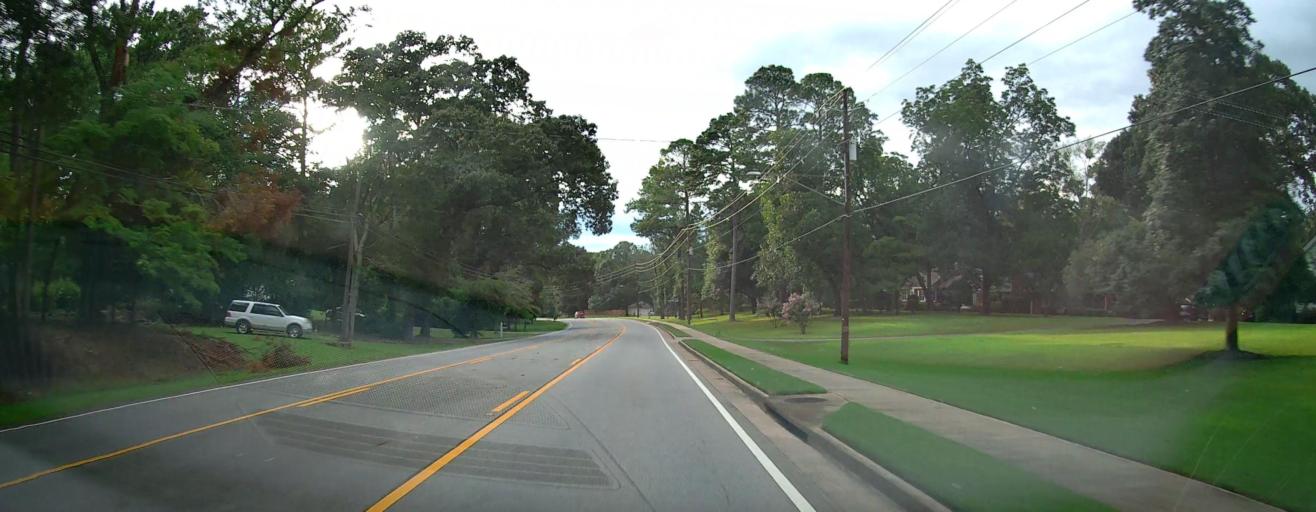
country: US
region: Georgia
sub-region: Houston County
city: Perry
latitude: 32.4578
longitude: -83.7182
